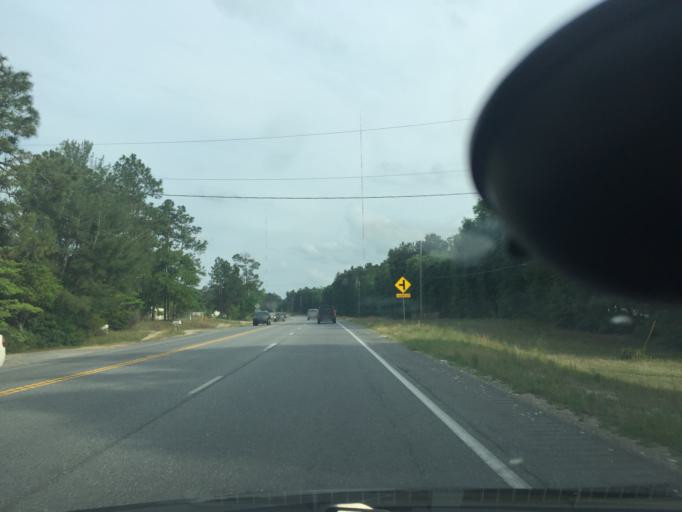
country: US
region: Georgia
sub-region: Chatham County
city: Bloomingdale
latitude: 32.0650
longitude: -81.3564
